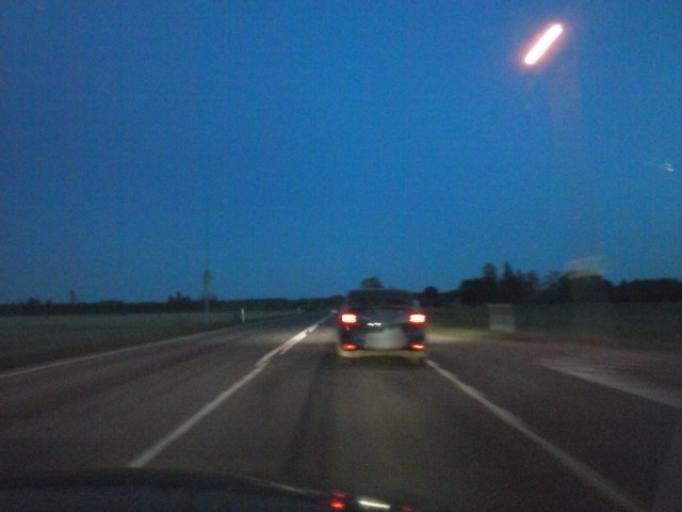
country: EE
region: Viljandimaa
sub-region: Vohma linn
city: Vohma
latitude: 58.7538
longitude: 25.5633
